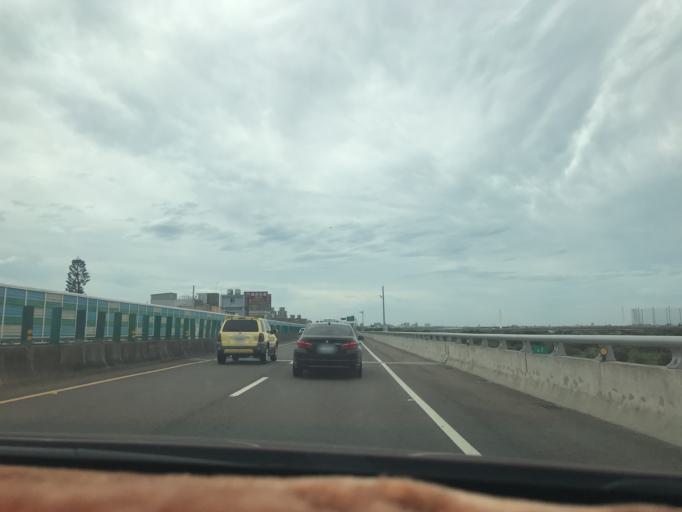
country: TW
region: Taiwan
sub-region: Hsinchu
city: Hsinchu
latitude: 24.8223
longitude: 120.9869
